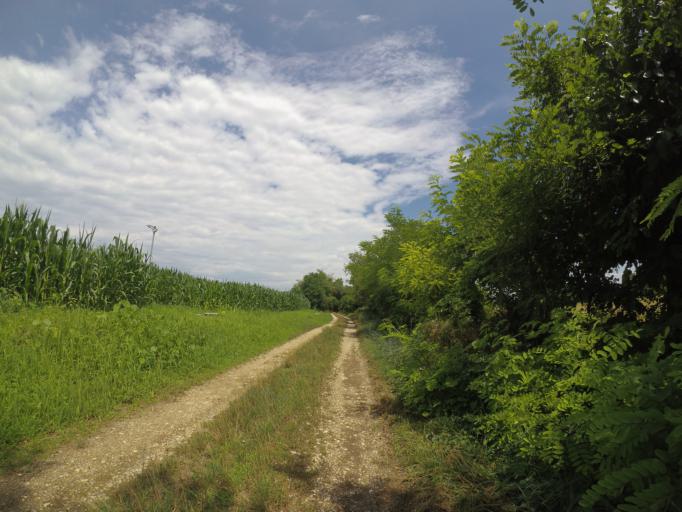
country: IT
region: Friuli Venezia Giulia
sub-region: Provincia di Udine
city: Bertiolo
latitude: 45.9630
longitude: 13.0590
